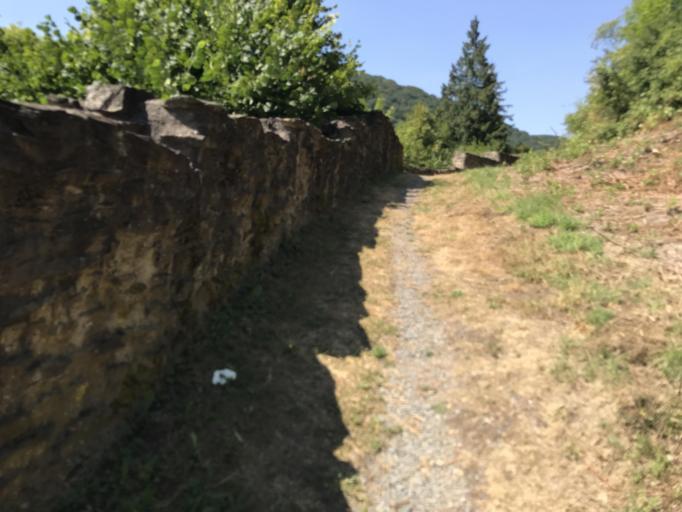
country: DE
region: Rheinland-Pfalz
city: Dausenau
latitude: 50.3285
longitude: 7.7621
